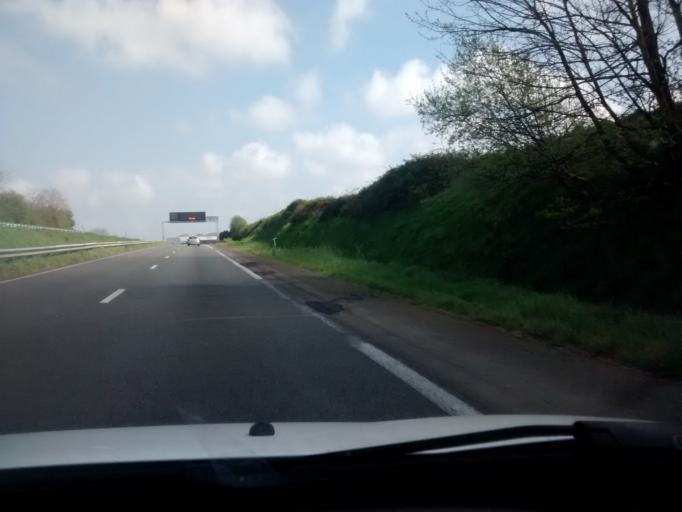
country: FR
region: Brittany
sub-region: Departement des Cotes-d'Armor
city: Tremuson
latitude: 48.5254
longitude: -2.8927
